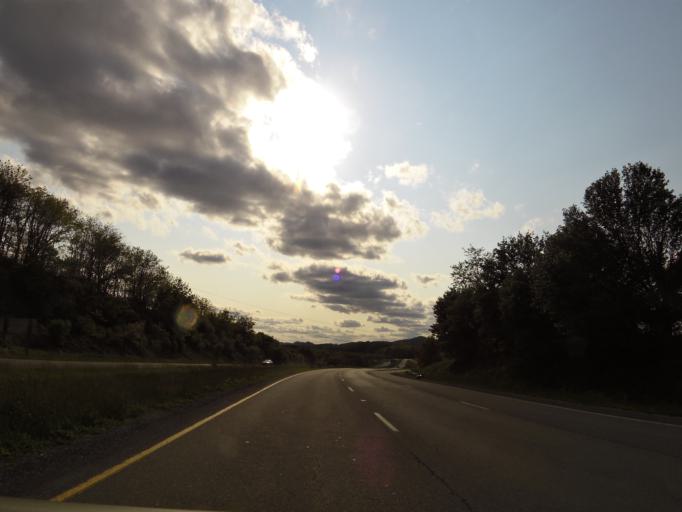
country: US
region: Virginia
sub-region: Tazewell County
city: Bluefield
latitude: 37.2363
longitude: -81.2543
